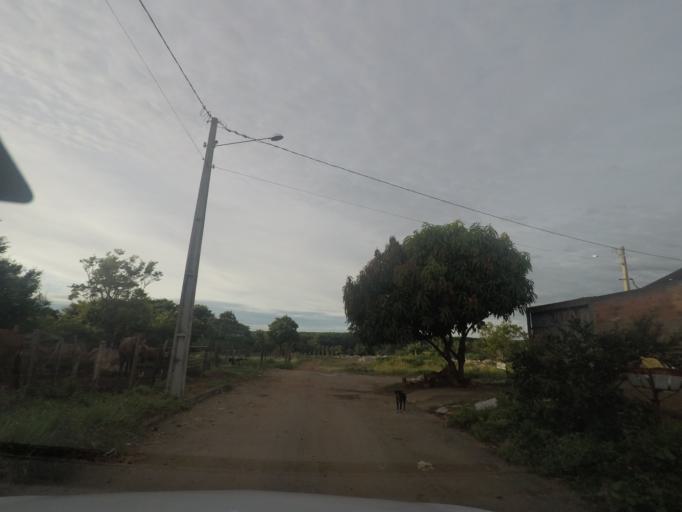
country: BR
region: Goias
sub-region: Trindade
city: Trindade
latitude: -16.7275
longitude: -49.4373
